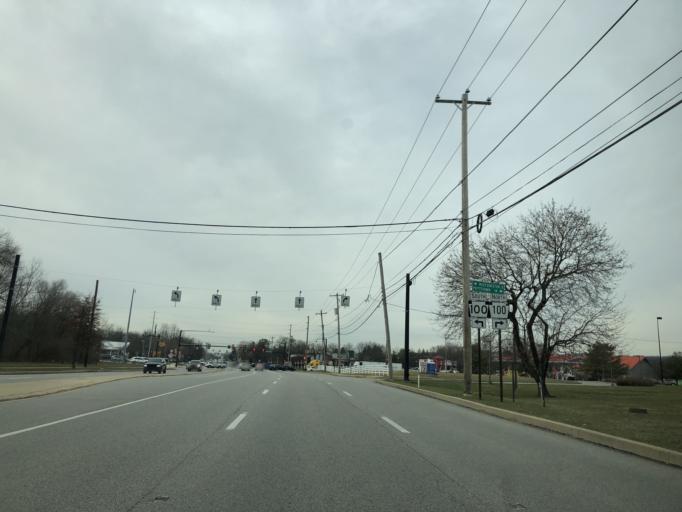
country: US
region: Pennsylvania
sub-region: Chester County
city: Exton
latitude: 40.0285
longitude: -75.6261
